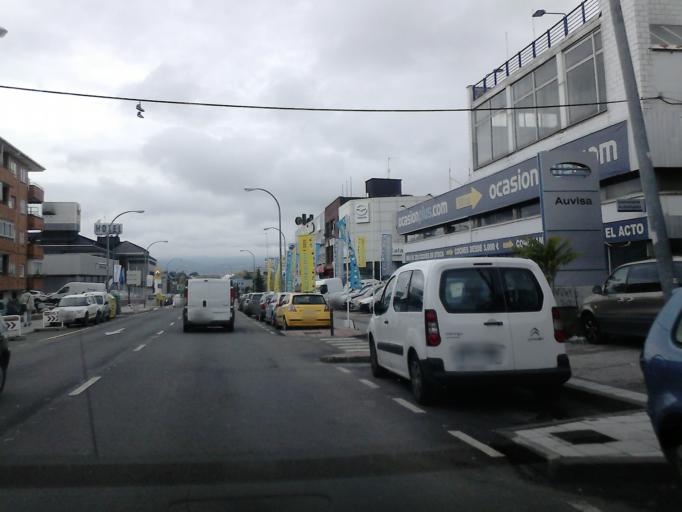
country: ES
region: Madrid
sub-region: Provincia de Madrid
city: Collado-Villalba
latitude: 40.6341
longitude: -4.0080
